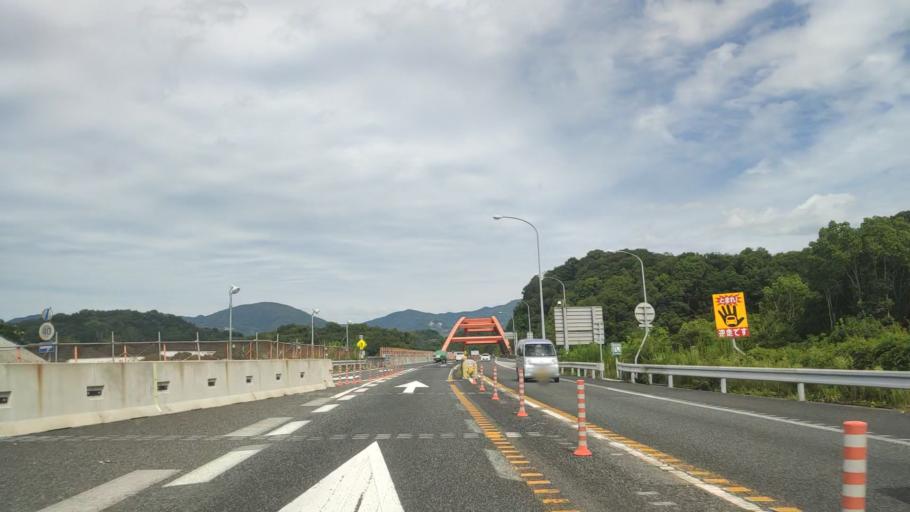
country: JP
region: Wakayama
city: Kainan
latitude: 34.0376
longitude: 135.2014
